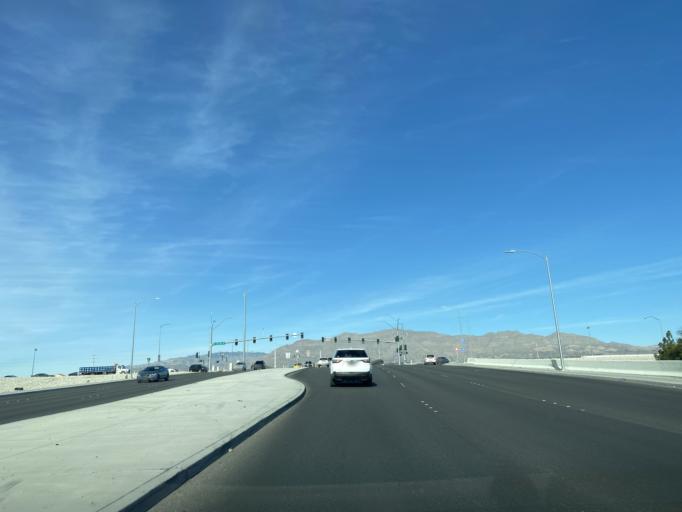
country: US
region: Nevada
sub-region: Clark County
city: North Las Vegas
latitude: 36.2730
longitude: -115.2066
